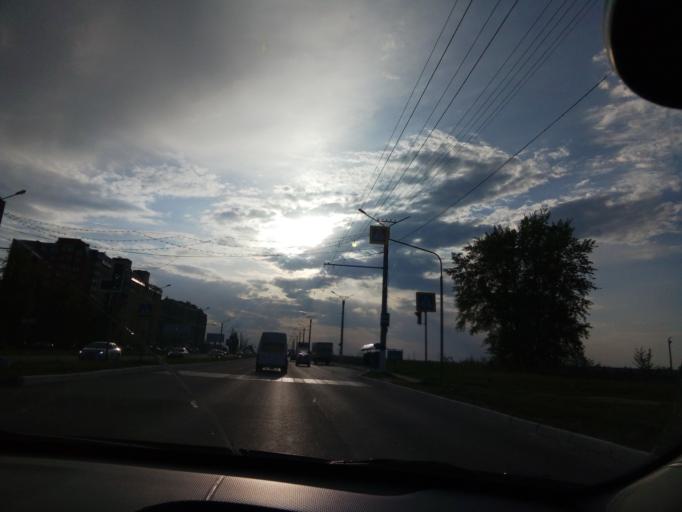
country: RU
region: Chuvashia
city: Novocheboksarsk
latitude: 56.1200
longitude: 47.4528
